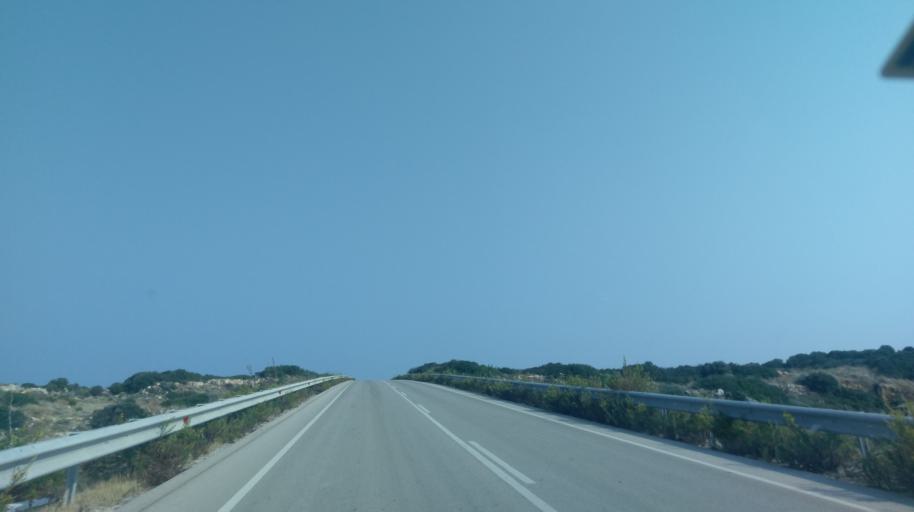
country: CY
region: Ammochostos
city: Trikomo
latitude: 35.4200
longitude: 33.8812
